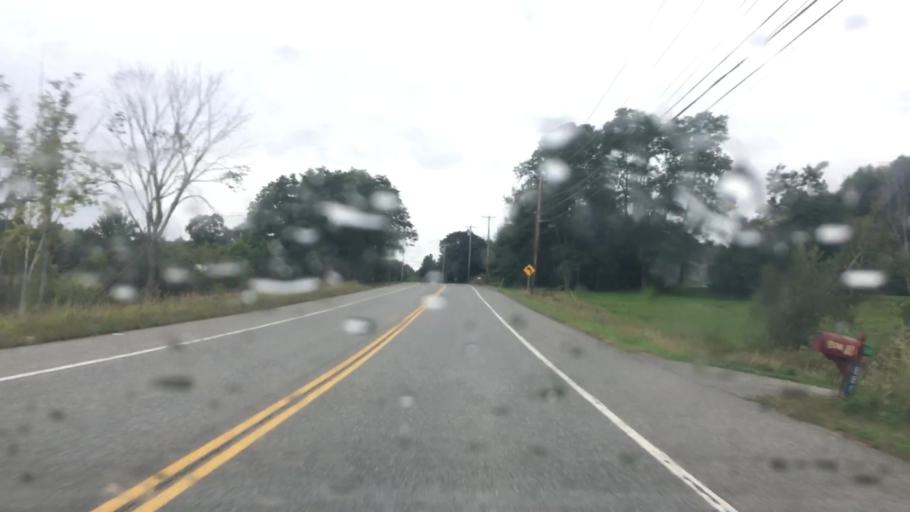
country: US
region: Maine
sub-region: Penobscot County
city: Orrington
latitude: 44.7171
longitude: -68.8271
